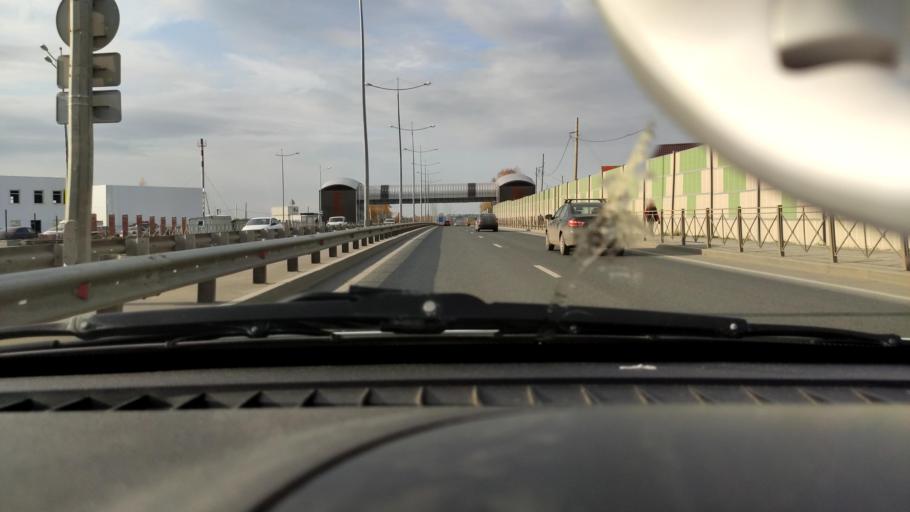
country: RU
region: Perm
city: Kondratovo
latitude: 57.9384
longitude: 56.0444
